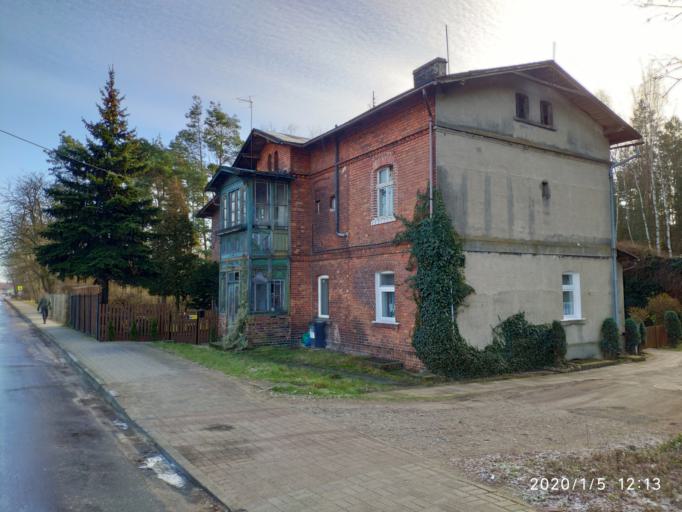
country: PL
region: Lubusz
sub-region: Powiat zielonogorski
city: Czerwiensk
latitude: 52.0151
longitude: 15.4089
